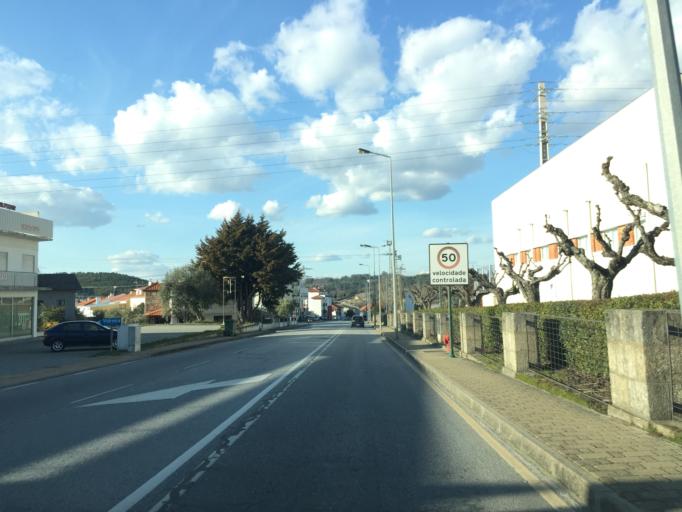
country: PT
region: Guarda
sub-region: Seia
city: Seia
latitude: 40.4226
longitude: -7.7137
